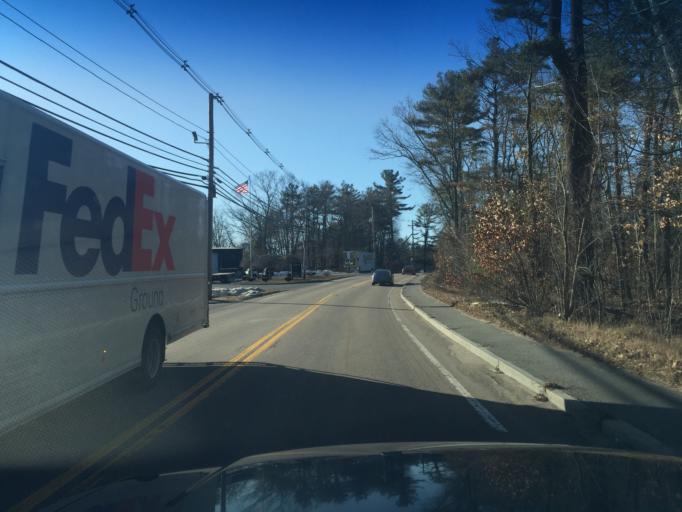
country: US
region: Massachusetts
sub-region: Norfolk County
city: Bellingham
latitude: 42.0878
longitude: -71.4967
